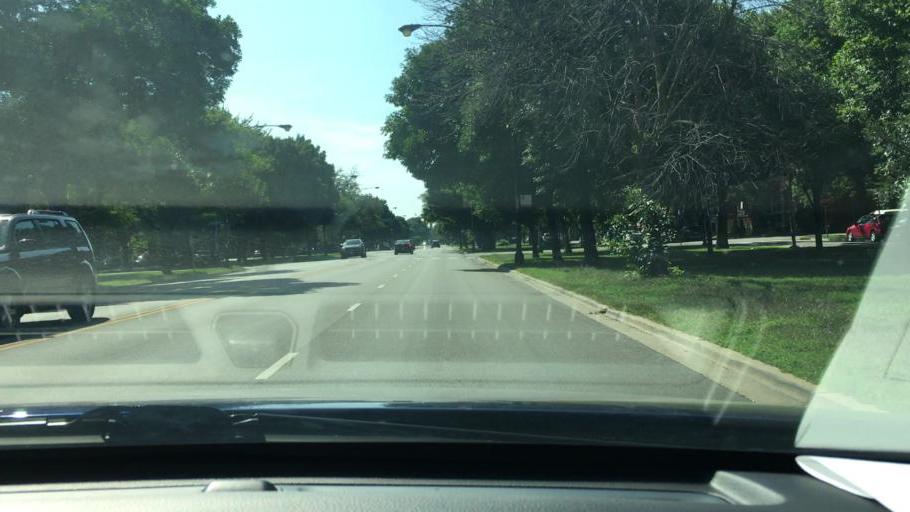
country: US
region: Illinois
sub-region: Cook County
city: Lincolnwood
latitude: 41.9285
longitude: -87.7004
